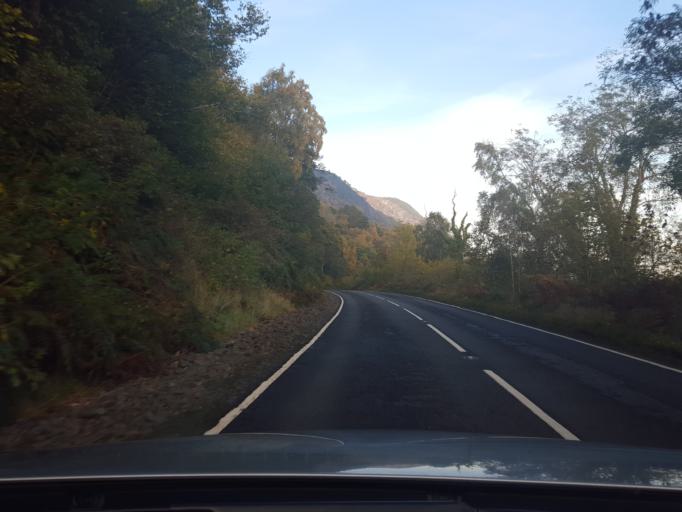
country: GB
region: Scotland
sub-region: Highland
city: Beauly
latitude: 57.3740
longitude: -4.3840
